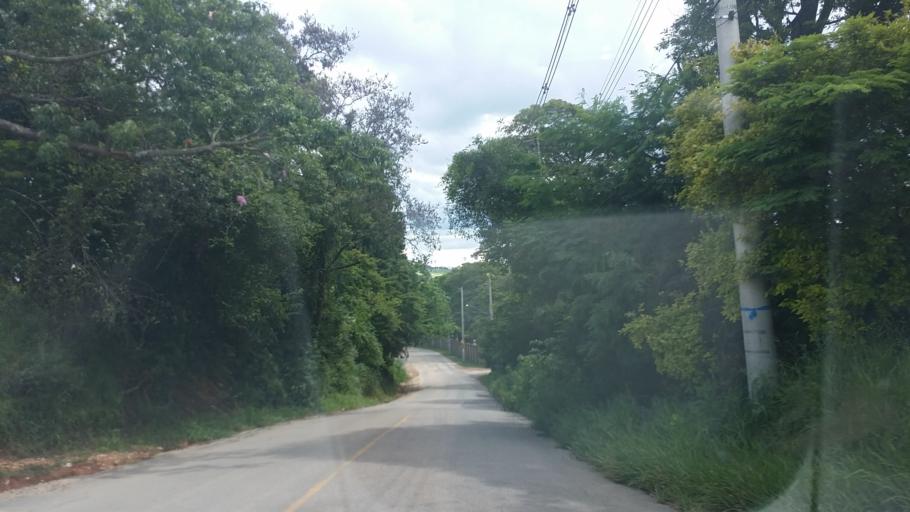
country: BR
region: Sao Paulo
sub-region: Itupeva
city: Itupeva
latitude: -23.1663
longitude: -47.0780
